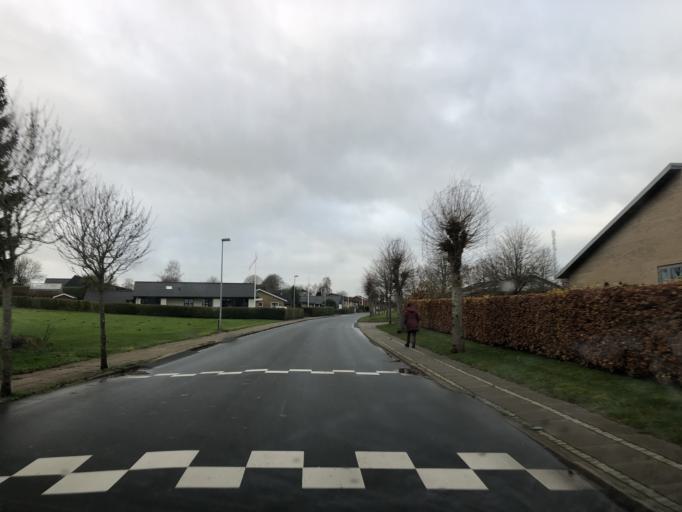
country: DK
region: North Denmark
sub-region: Vesthimmerland Kommune
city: Alestrup
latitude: 56.5913
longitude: 9.6266
